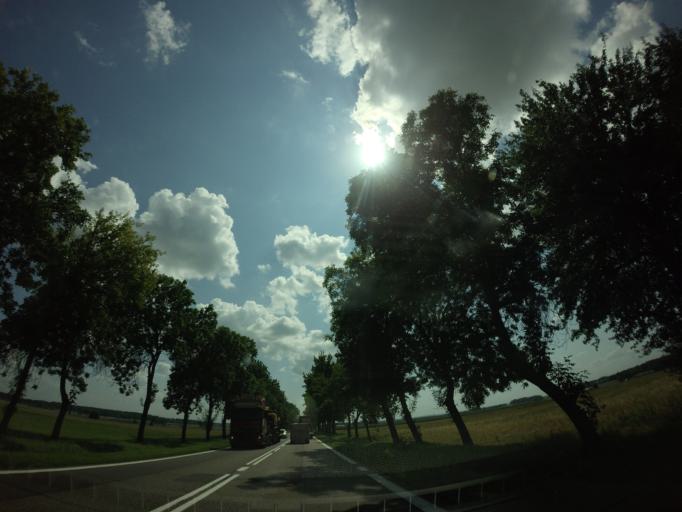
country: PL
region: Podlasie
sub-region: Powiat lomzynski
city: Piatnica
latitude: 53.2653
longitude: 22.1281
